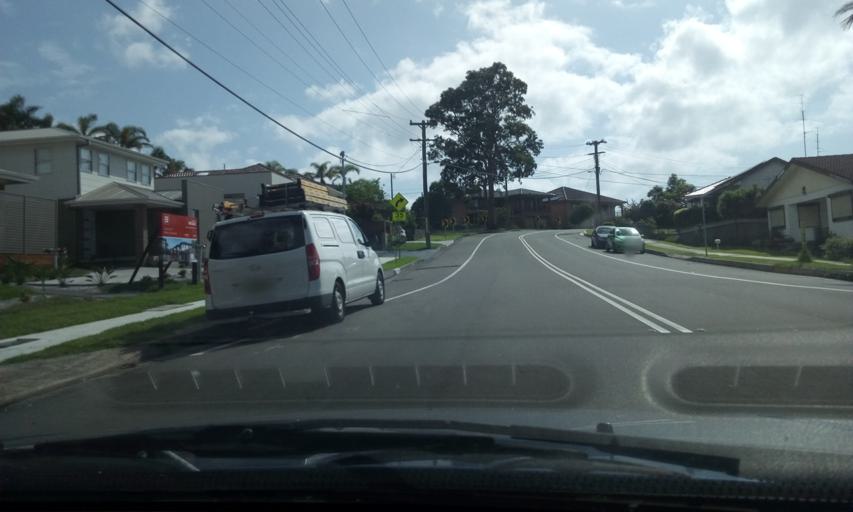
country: AU
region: New South Wales
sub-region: Wollongong
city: Corrimal
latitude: -34.3745
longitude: 150.8910
